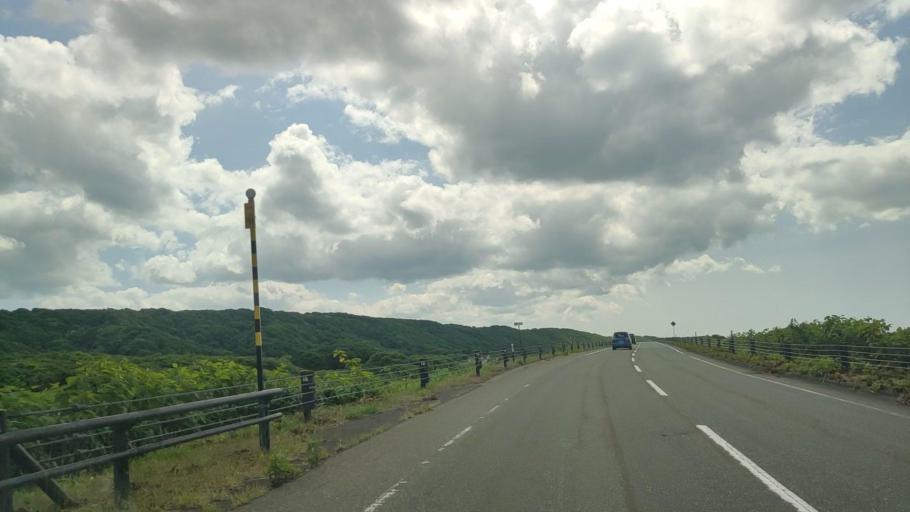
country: JP
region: Hokkaido
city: Wakkanai
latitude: 45.3006
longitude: 141.6240
